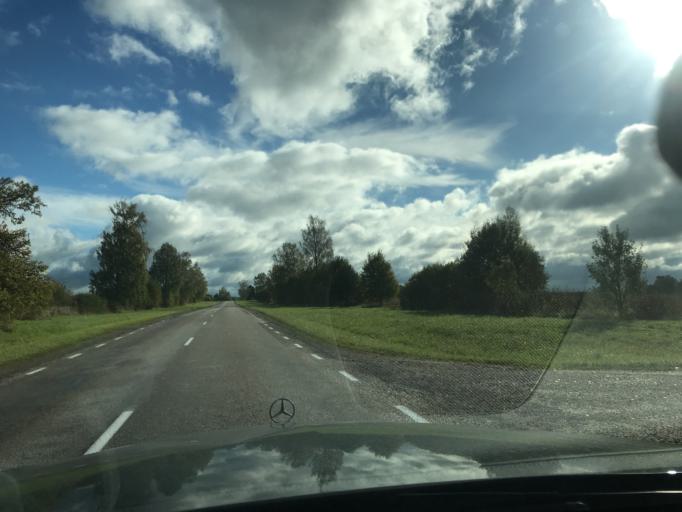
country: EE
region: Valgamaa
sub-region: Torva linn
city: Torva
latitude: 58.0108
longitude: 26.1853
